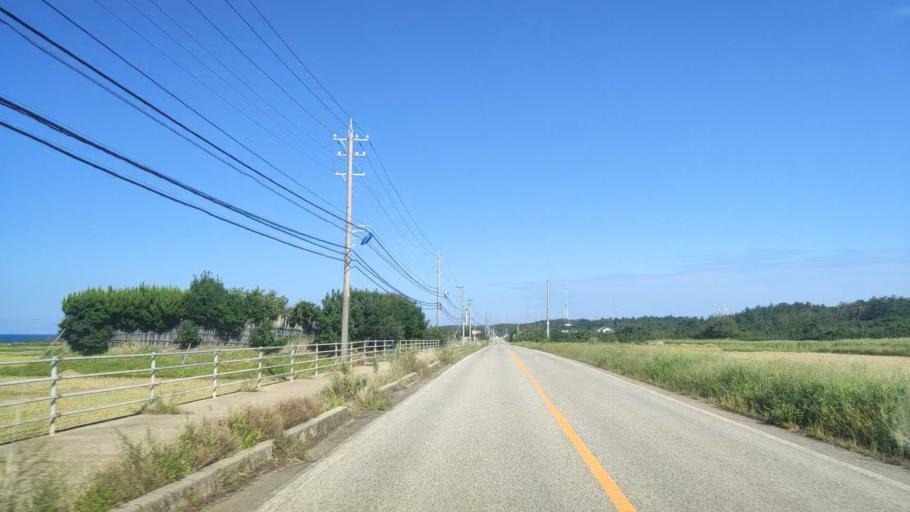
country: JP
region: Ishikawa
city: Hakui
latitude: 37.0409
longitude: 136.7413
